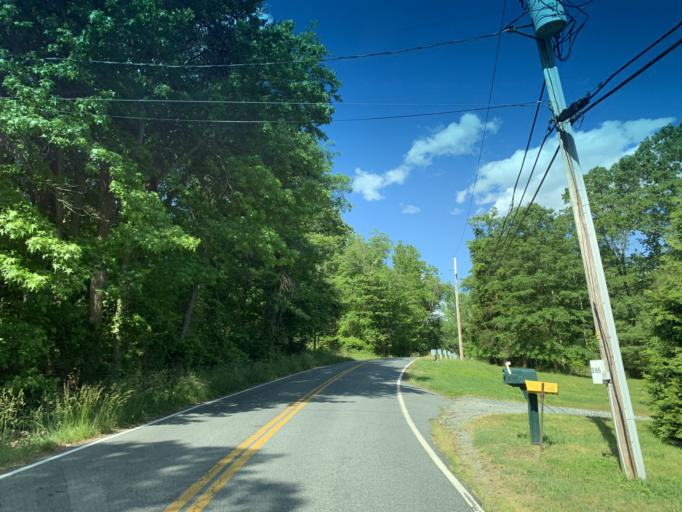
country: US
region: Maryland
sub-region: Cecil County
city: Charlestown
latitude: 39.5440
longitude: -75.9354
